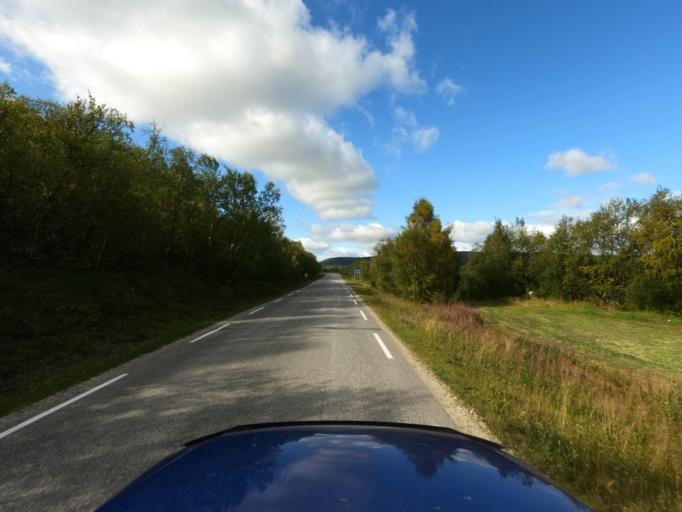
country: NO
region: Finnmark Fylke
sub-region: Karasjok
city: Karasjohka
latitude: 69.4594
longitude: 25.5398
